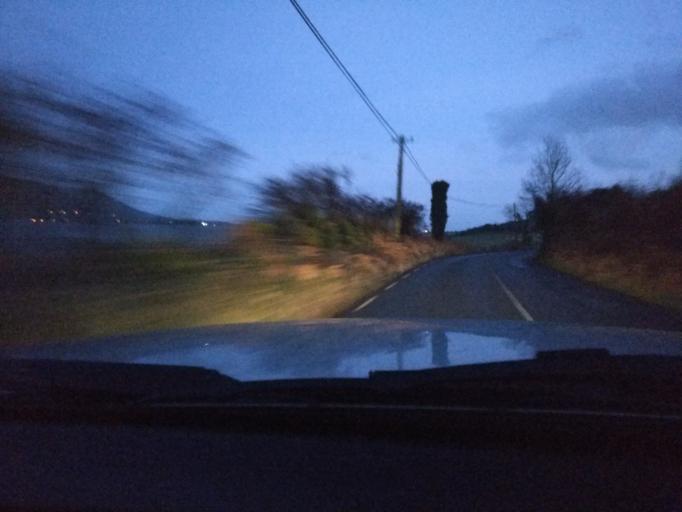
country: GB
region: Northern Ireland
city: Rostrevor
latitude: 54.0681
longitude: -6.2239
